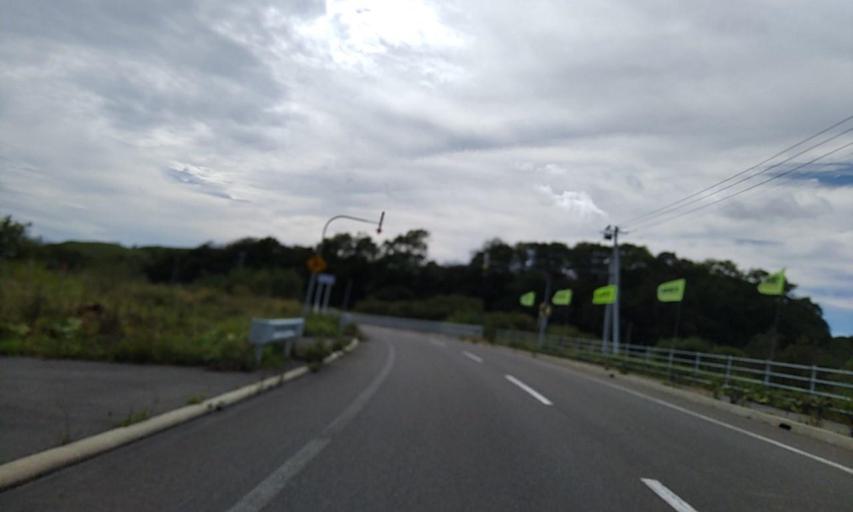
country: JP
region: Hokkaido
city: Kushiro
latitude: 42.8064
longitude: 143.8152
